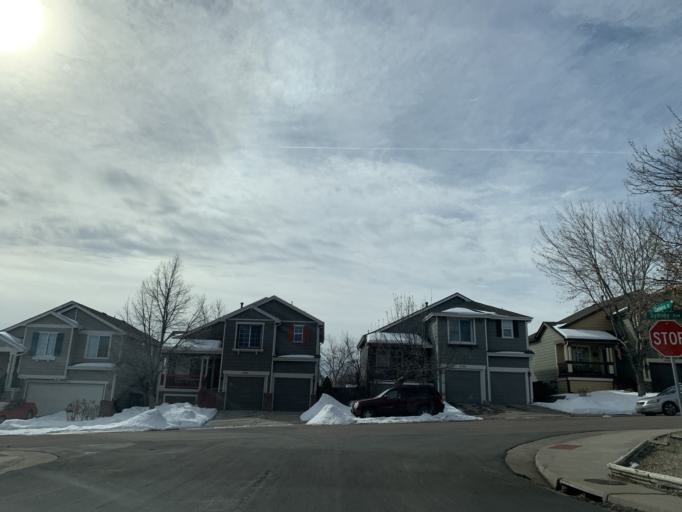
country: US
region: Colorado
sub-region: Douglas County
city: Carriage Club
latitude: 39.5396
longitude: -104.9284
